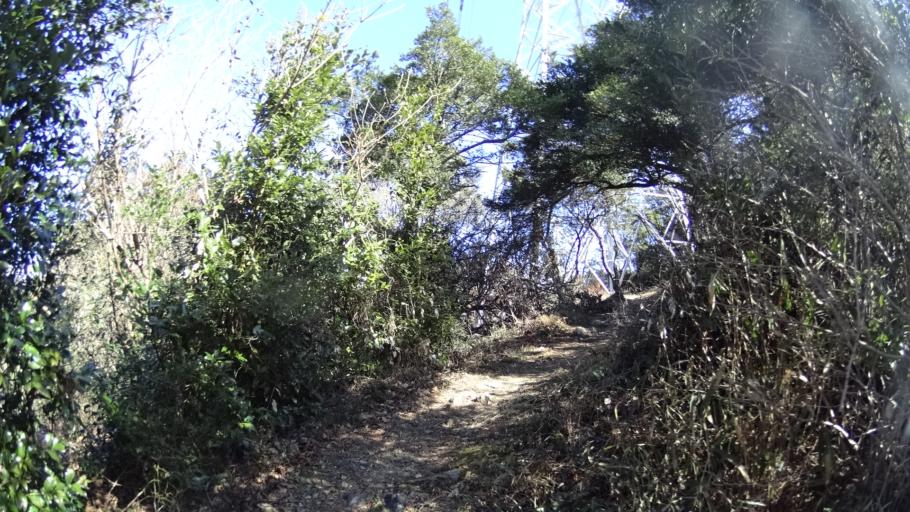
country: JP
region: Shizuoka
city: Kosai-shi
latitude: 34.7558
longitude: 137.4756
